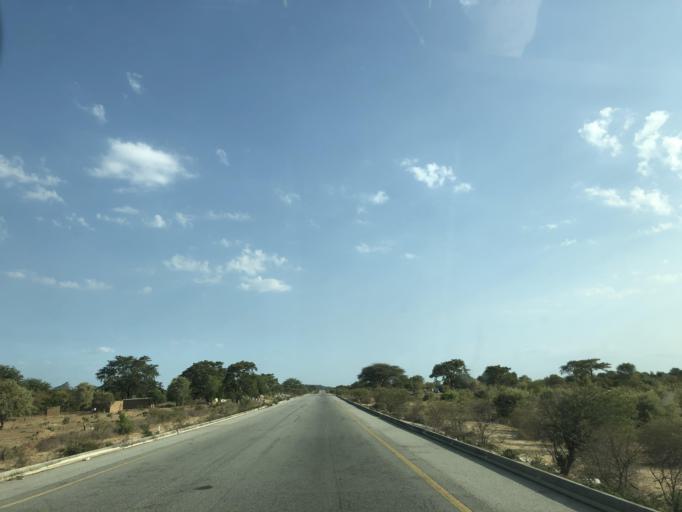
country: AO
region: Benguela
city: Benguela
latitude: -13.2117
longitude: 13.7646
